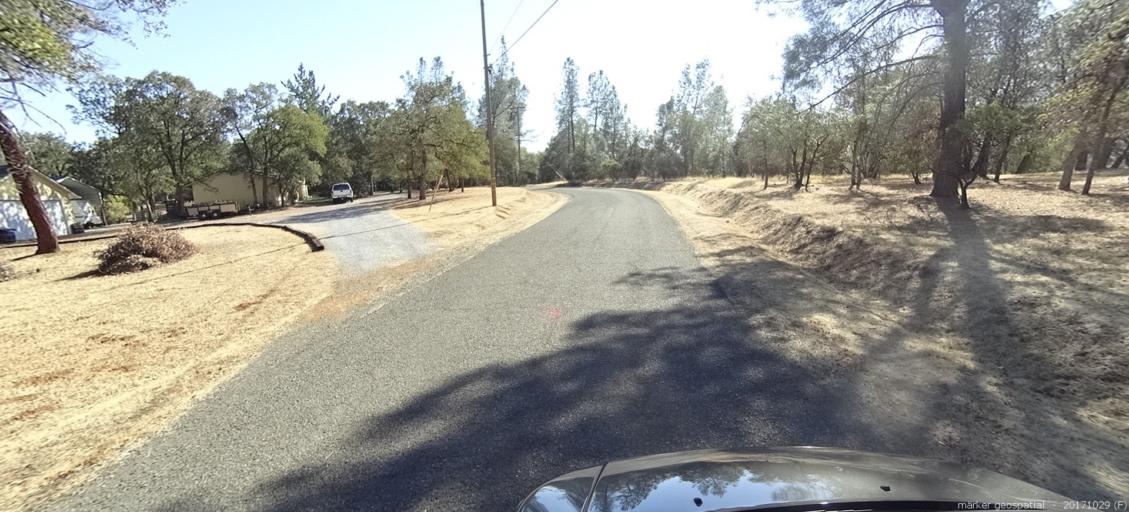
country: US
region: California
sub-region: Shasta County
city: Anderson
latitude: 40.4759
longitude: -122.3587
